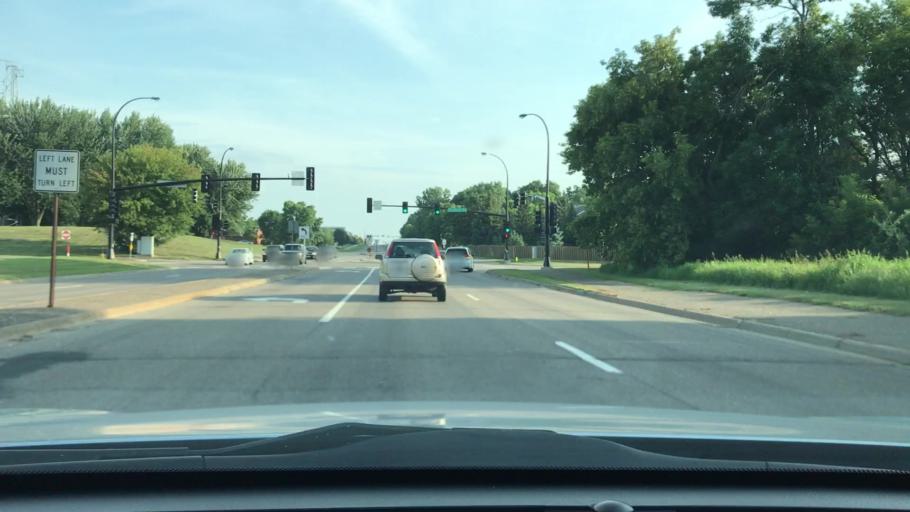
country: US
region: Minnesota
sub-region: Hennepin County
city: Plymouth
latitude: 45.0276
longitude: -93.4818
